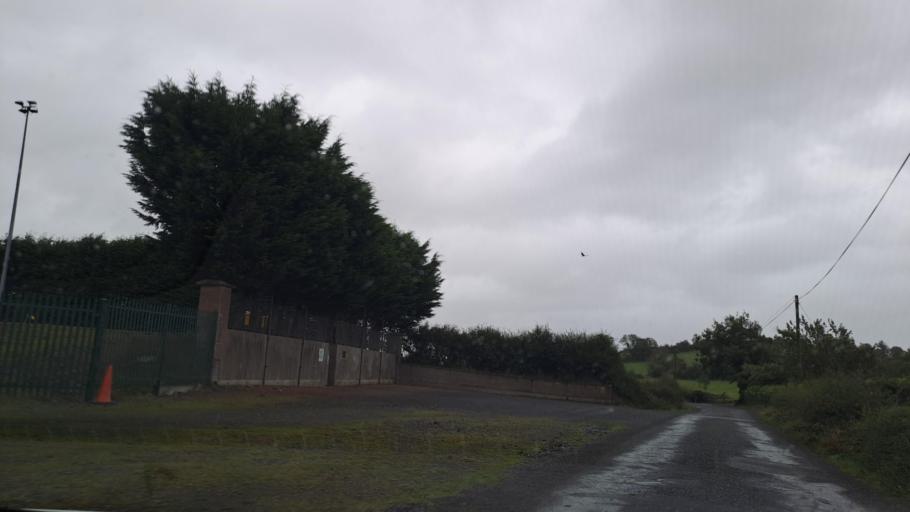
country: IE
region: Ulster
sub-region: An Cabhan
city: Kingscourt
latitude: 54.0079
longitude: -6.8228
